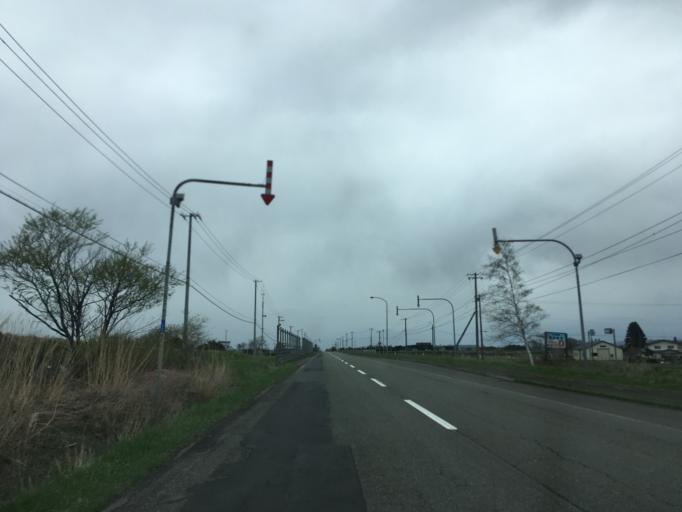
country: JP
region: Hokkaido
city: Chitose
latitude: 42.9247
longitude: 141.8082
